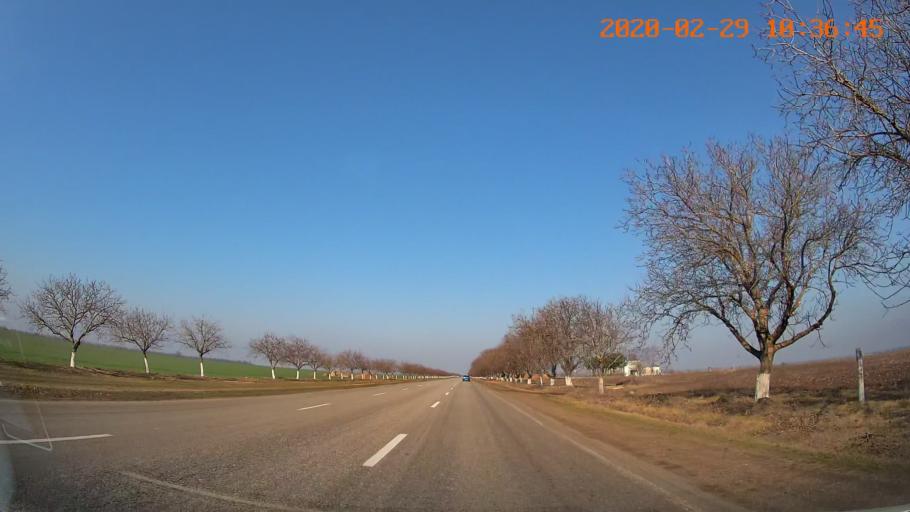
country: MD
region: Anenii Noi
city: Varnita
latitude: 46.9989
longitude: 29.5002
